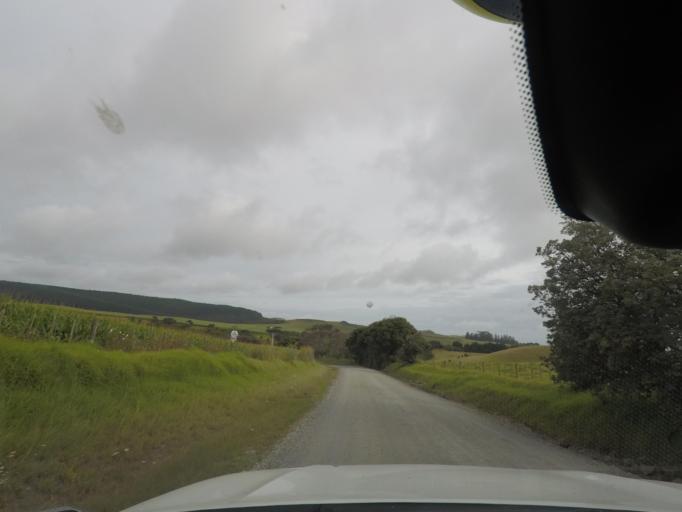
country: NZ
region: Auckland
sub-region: Auckland
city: Parakai
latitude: -36.4736
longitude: 174.2575
